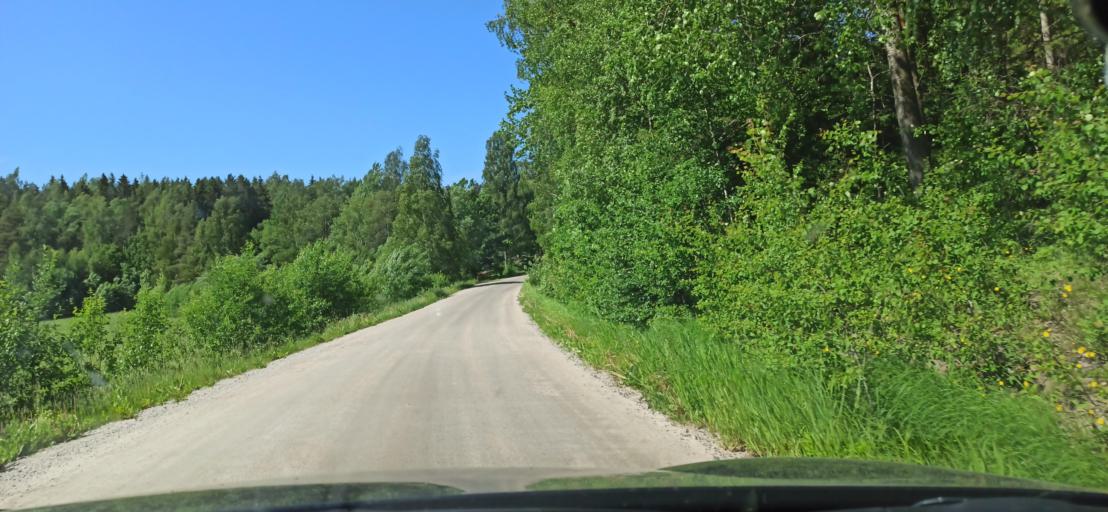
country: FI
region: Varsinais-Suomi
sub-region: Turku
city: Sauvo
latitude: 60.3814
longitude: 22.6605
